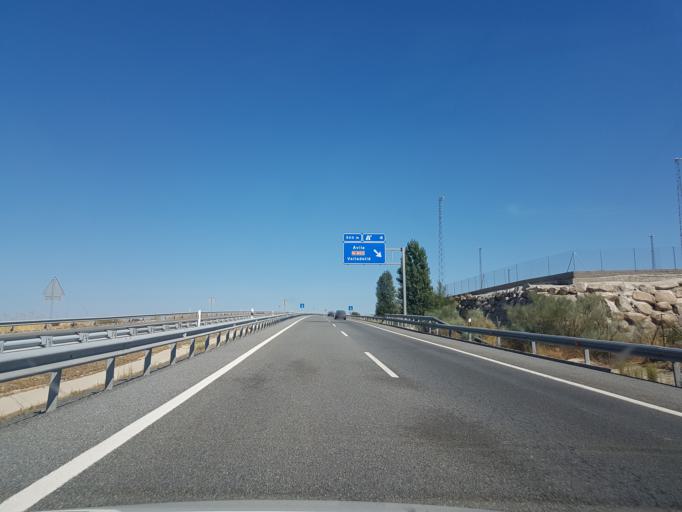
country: ES
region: Castille and Leon
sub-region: Provincia de Avila
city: Avila
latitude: 40.6758
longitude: -4.6970
